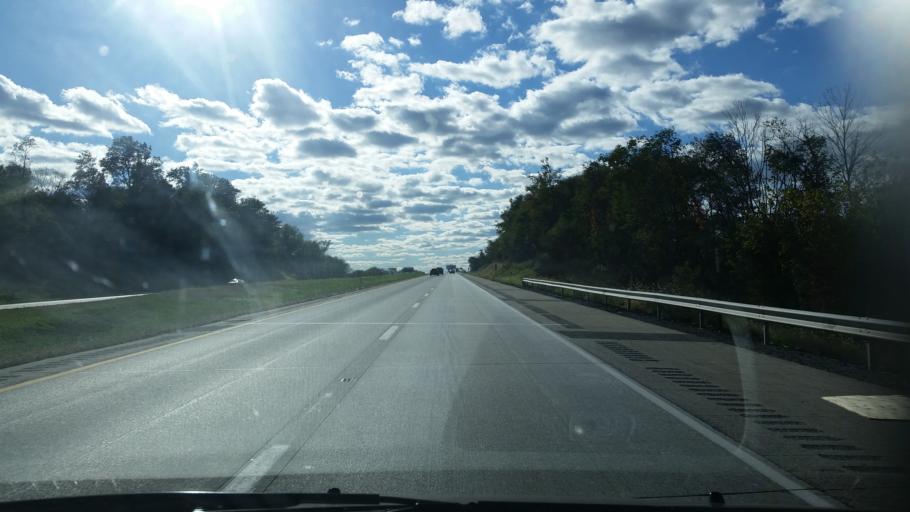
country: US
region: Pennsylvania
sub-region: Lebanon County
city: Fredericksburg
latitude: 40.4533
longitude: -76.3932
